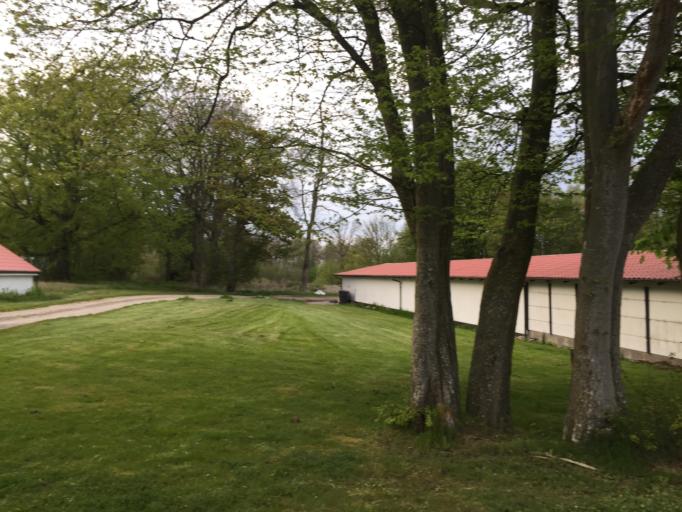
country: DK
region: North Denmark
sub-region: Alborg Kommune
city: Frejlev
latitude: 57.0054
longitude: 9.7742
